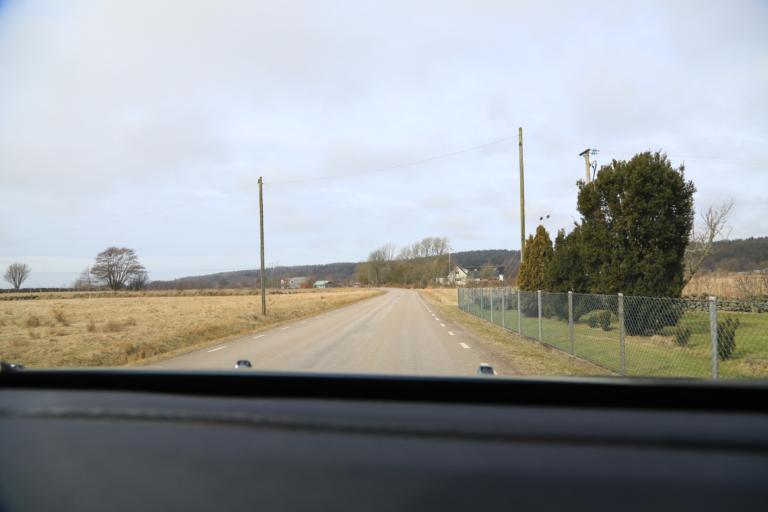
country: SE
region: Halland
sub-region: Varbergs Kommun
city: Veddige
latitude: 57.2271
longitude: 12.2460
